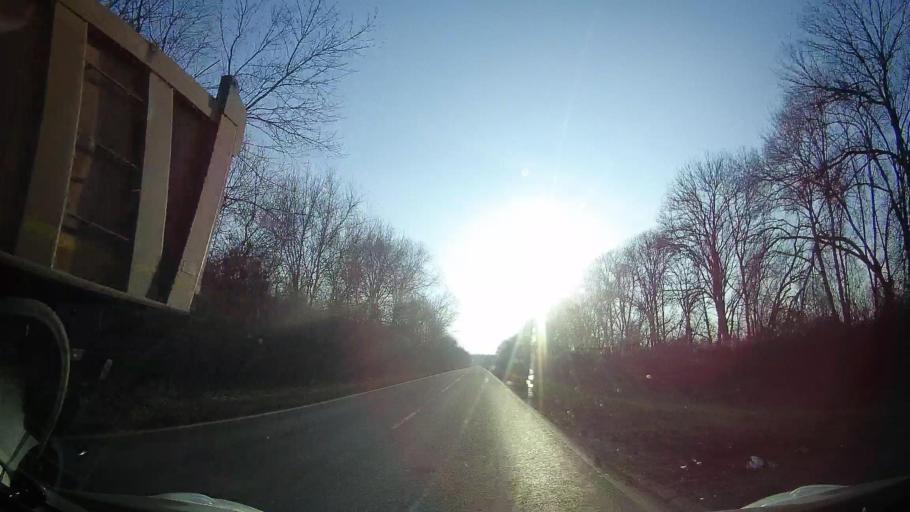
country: RU
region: Rostov
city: Ol'ginskaya
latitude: 47.1673
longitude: 39.9403
